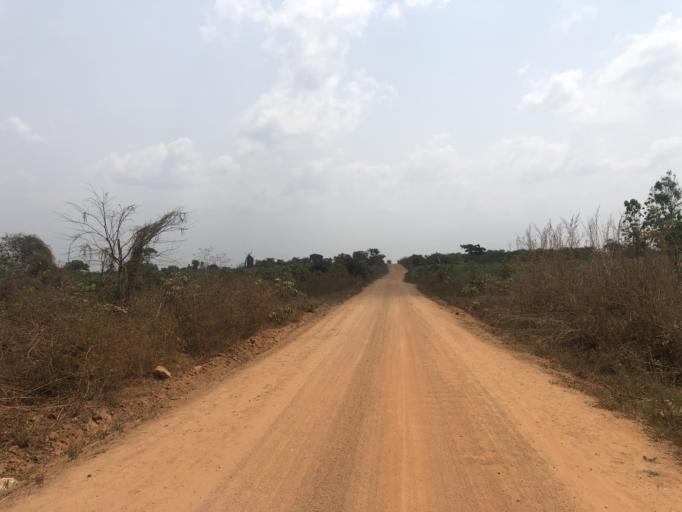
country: NG
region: Osun
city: Bode Osi
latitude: 7.7971
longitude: 4.1766
